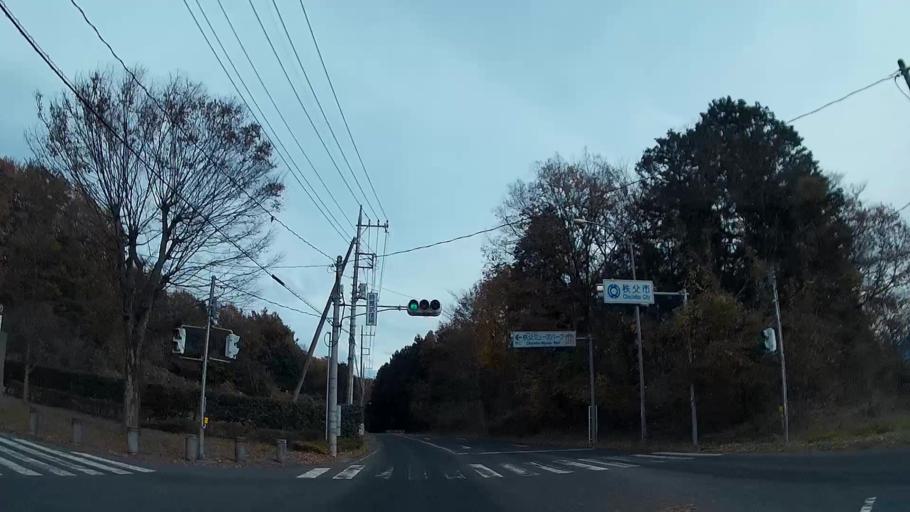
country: JP
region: Saitama
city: Chichibu
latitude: 35.9821
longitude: 139.0438
